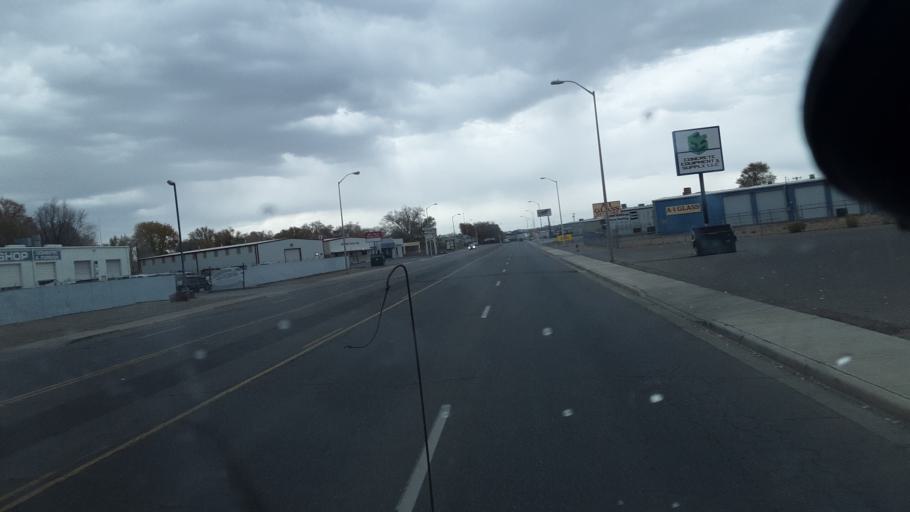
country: US
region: New Mexico
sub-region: San Juan County
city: Farmington
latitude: 36.7354
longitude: -108.1828
